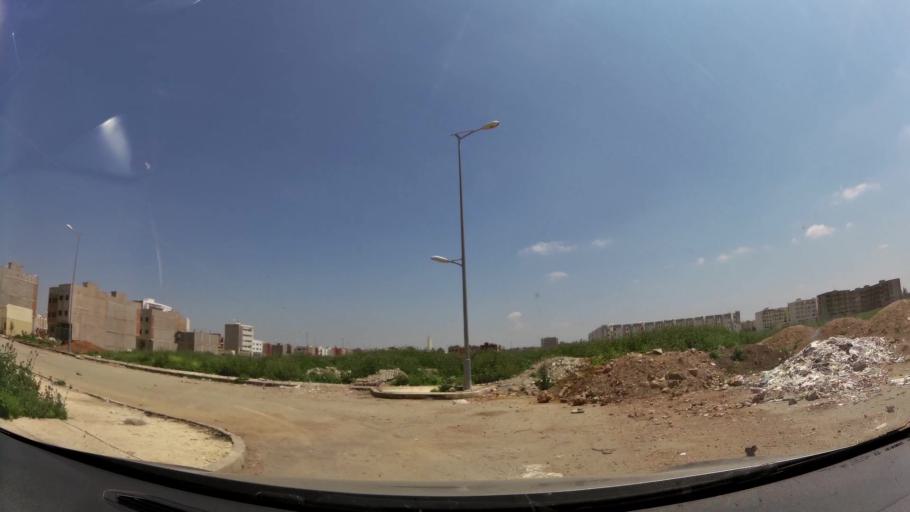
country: MA
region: Fes-Boulemane
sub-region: Fes
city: Fes
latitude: 34.0226
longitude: -5.0619
